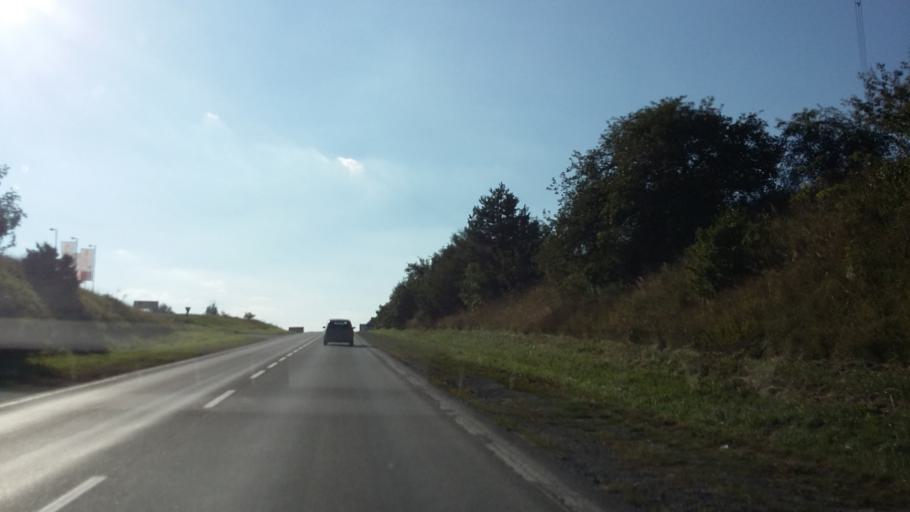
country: CZ
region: South Moravian
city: Troubsko
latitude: 49.1751
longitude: 16.5164
